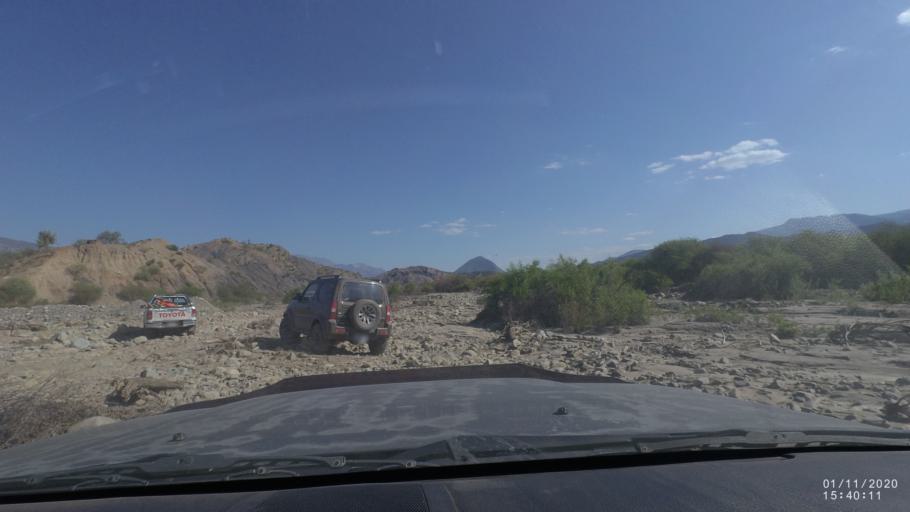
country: BO
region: Chuquisaca
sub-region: Provincia Zudanez
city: Mojocoya
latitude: -18.6777
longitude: -64.5024
